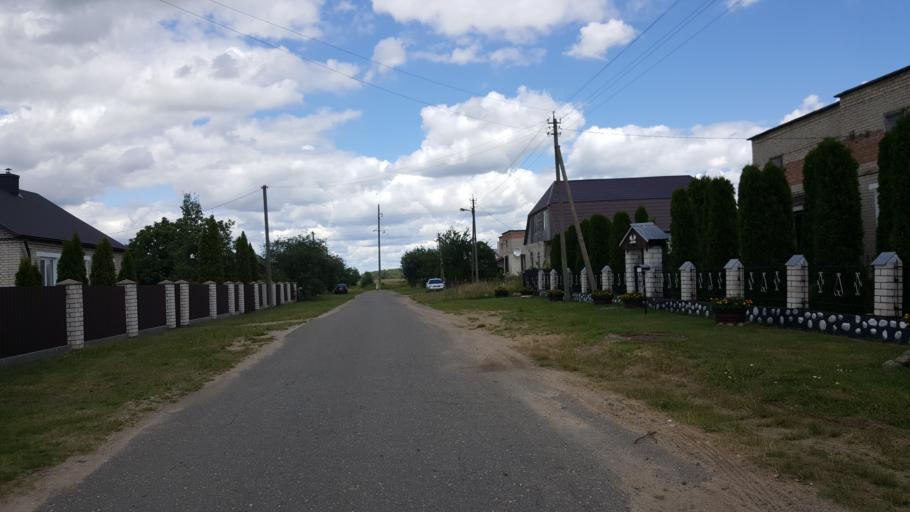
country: BY
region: Brest
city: Kamyanyets
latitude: 52.3191
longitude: 23.9214
